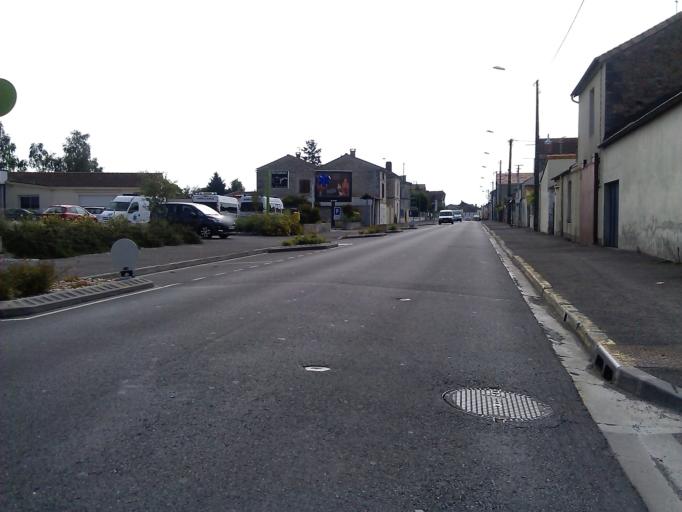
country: FR
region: Poitou-Charentes
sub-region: Departement de la Charente
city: Angouleme
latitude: 45.6623
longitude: 0.1346
